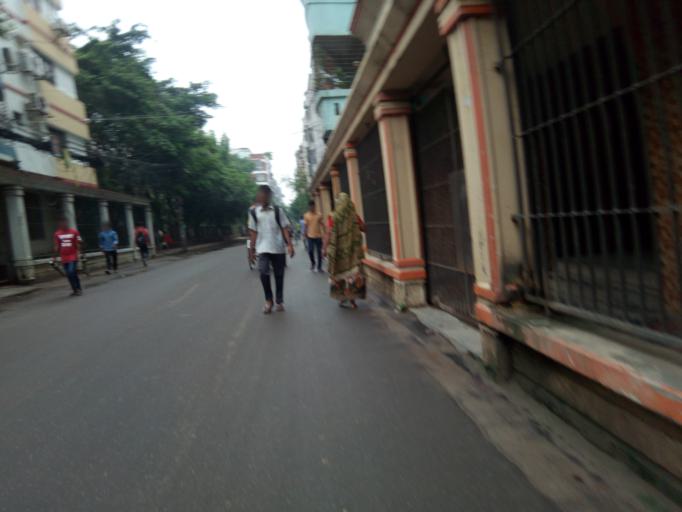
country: BD
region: Dhaka
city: Paltan
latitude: 23.7872
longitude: 90.4005
